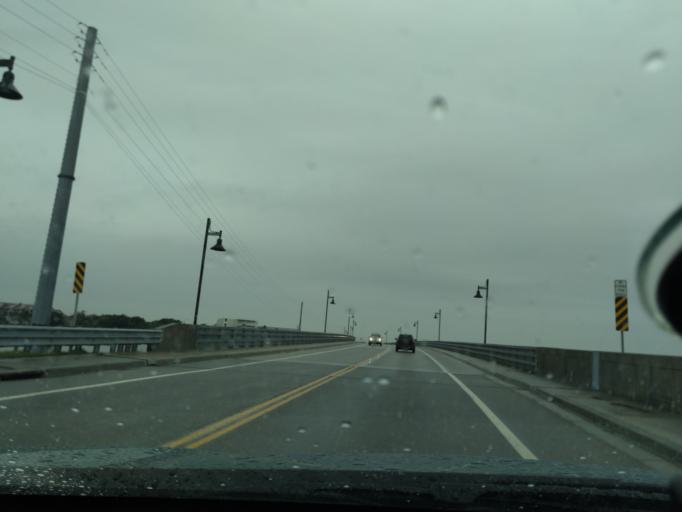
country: US
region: South Carolina
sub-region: Charleston County
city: Folly Beach
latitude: 32.6599
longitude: -79.9428
